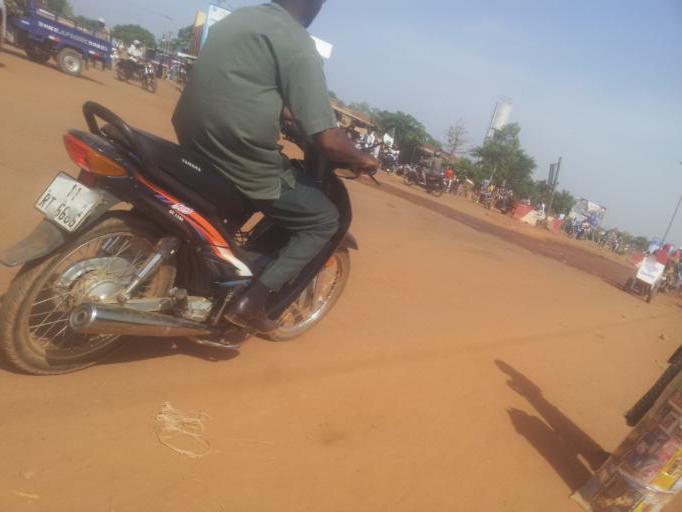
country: BF
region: Centre
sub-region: Kadiogo Province
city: Ouagadougou
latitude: 12.3830
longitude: -1.5526
